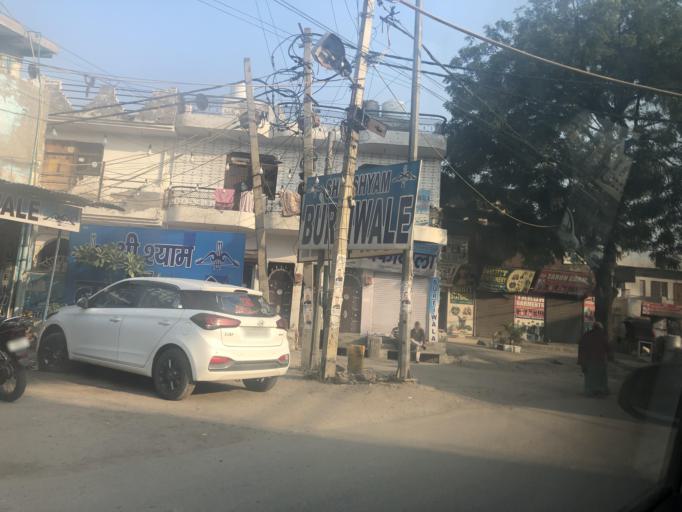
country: IN
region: Haryana
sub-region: Gurgaon
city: Gurgaon
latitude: 28.5594
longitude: 77.0034
